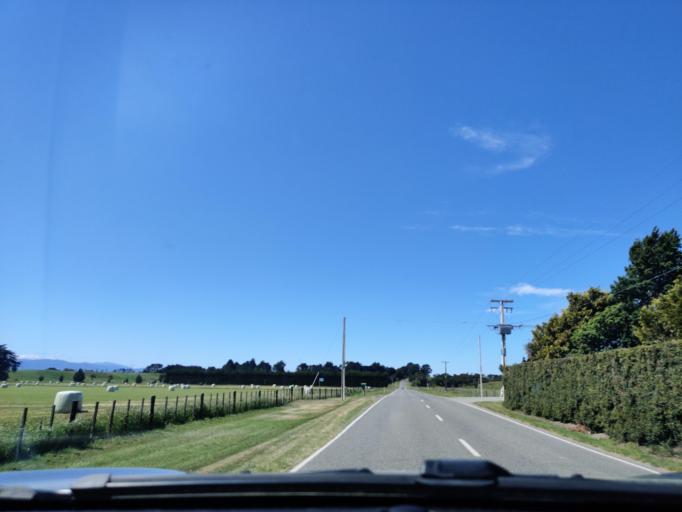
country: NZ
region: Wellington
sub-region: Upper Hutt City
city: Upper Hutt
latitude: -41.3174
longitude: 175.2575
